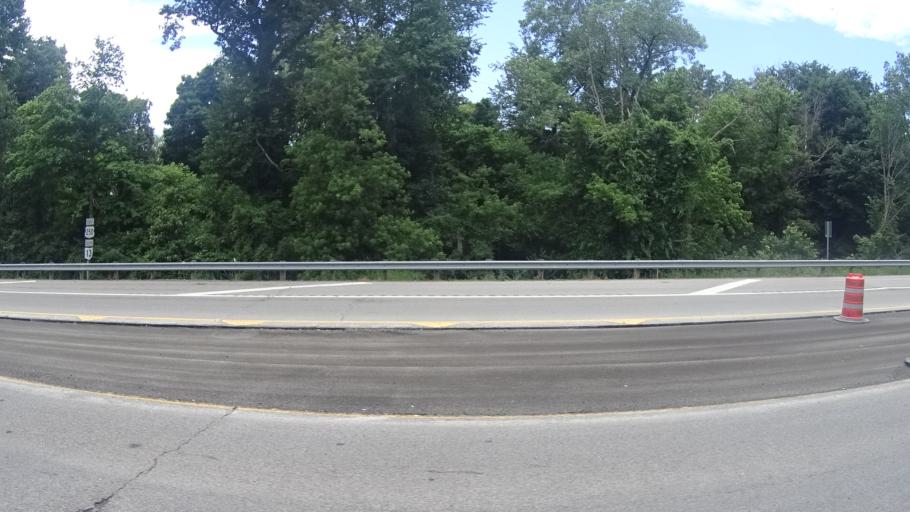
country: US
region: Ohio
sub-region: Erie County
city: Milan
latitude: 41.2952
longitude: -82.6087
